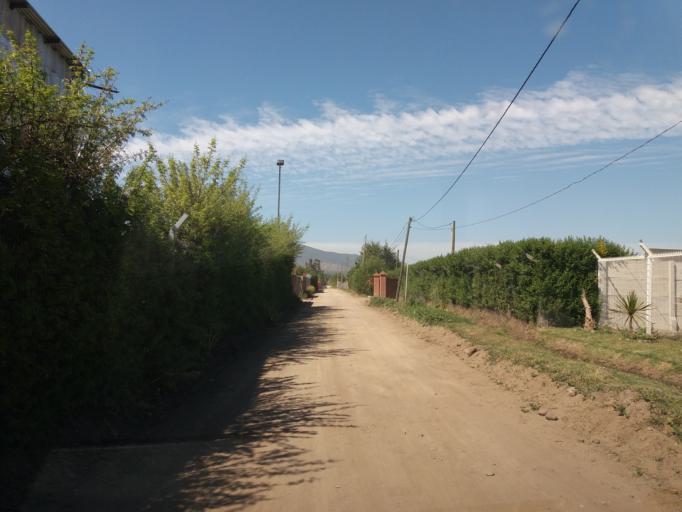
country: CL
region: Valparaiso
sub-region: Provincia de Quillota
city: Quillota
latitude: -32.8684
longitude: -71.2235
